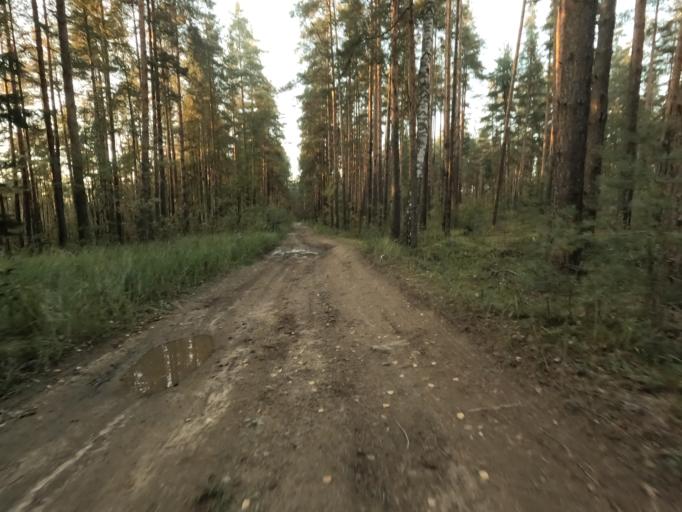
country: RU
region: Leningrad
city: Otradnoye
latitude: 59.8414
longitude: 30.8031
